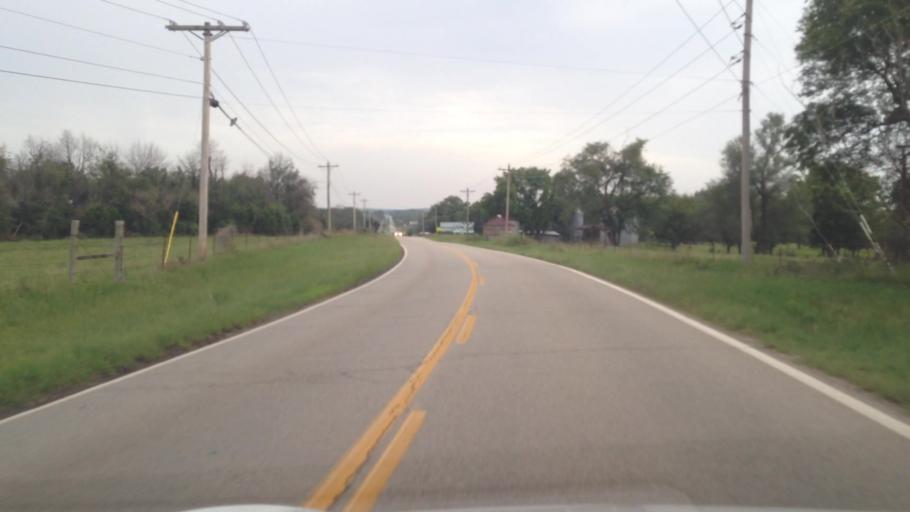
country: US
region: Oklahoma
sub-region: Delaware County
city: Cleora
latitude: 36.5824
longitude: -94.9708
